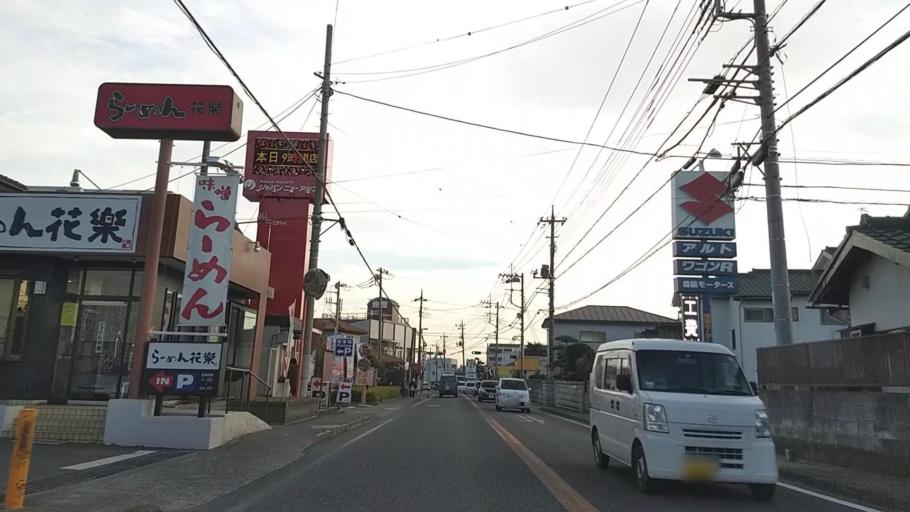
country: JP
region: Kanagawa
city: Atsugi
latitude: 35.4741
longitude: 139.3454
